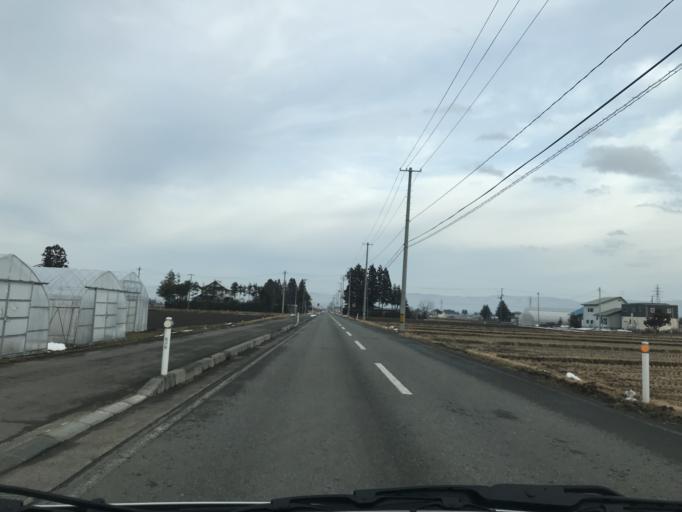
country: JP
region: Iwate
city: Mizusawa
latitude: 39.1356
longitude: 141.0916
